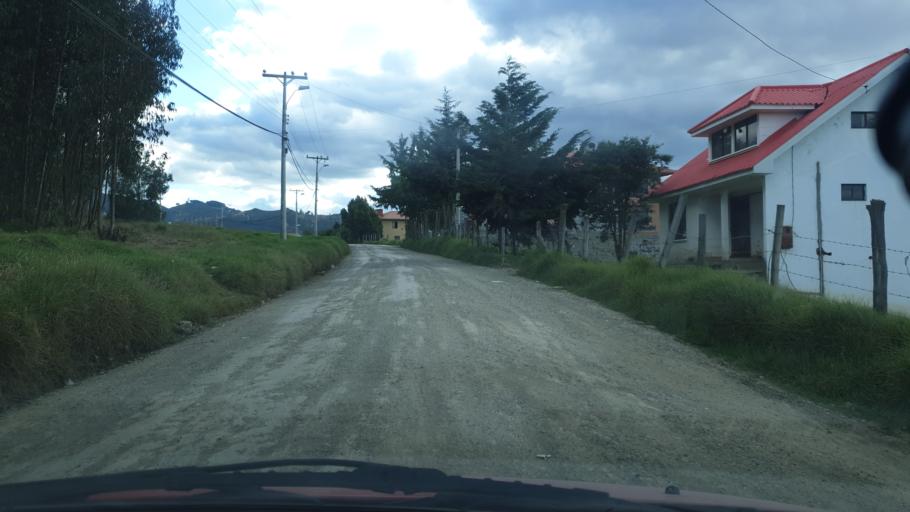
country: EC
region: Azuay
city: Cuenca
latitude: -2.9243
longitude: -78.9716
